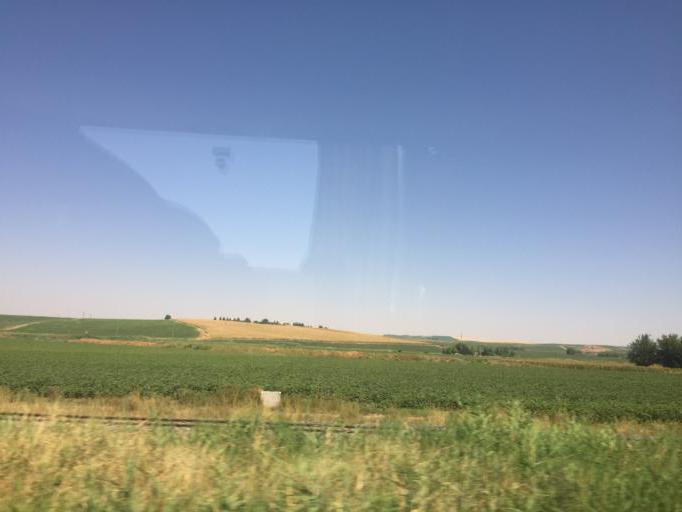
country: TR
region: Diyarbakir
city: Tepe
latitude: 37.8507
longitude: 40.7501
